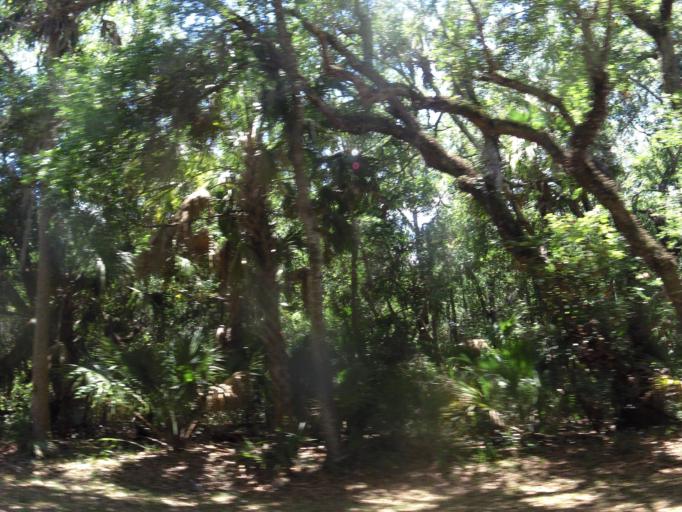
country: US
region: Florida
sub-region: Flagler County
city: Palm Coast
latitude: 29.6289
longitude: -81.2070
